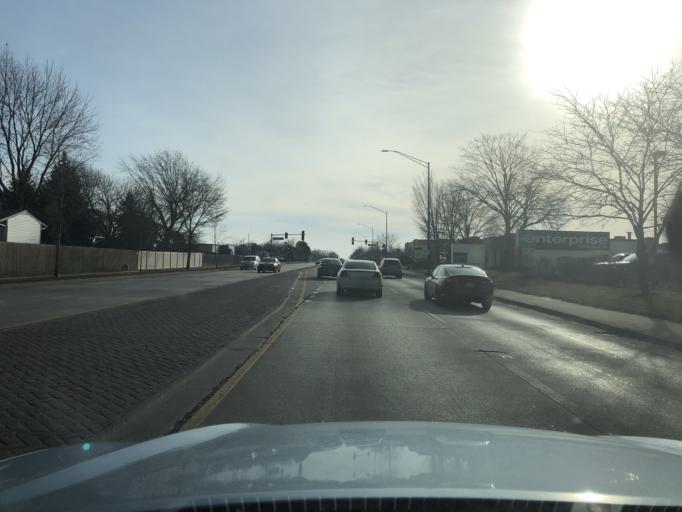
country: US
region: Illinois
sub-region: Cook County
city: Schaumburg
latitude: 42.0097
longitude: -88.0800
